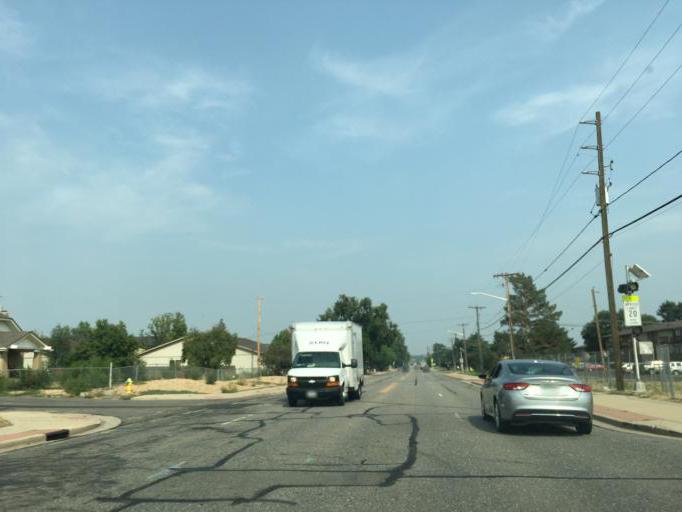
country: US
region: Colorado
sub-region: Jefferson County
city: Arvada
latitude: 39.7781
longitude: -105.1166
